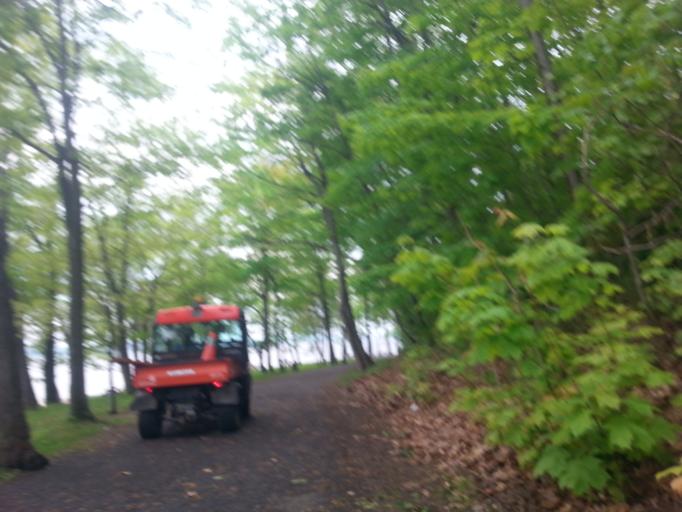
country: CA
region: Quebec
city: L'Ancienne-Lorette
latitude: 46.7494
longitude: -71.3225
